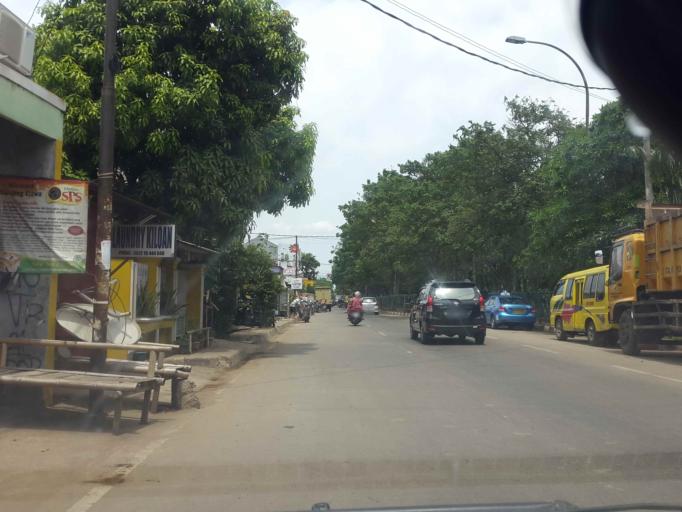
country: ID
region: Banten
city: Tangerang
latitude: -6.1575
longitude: 106.6323
